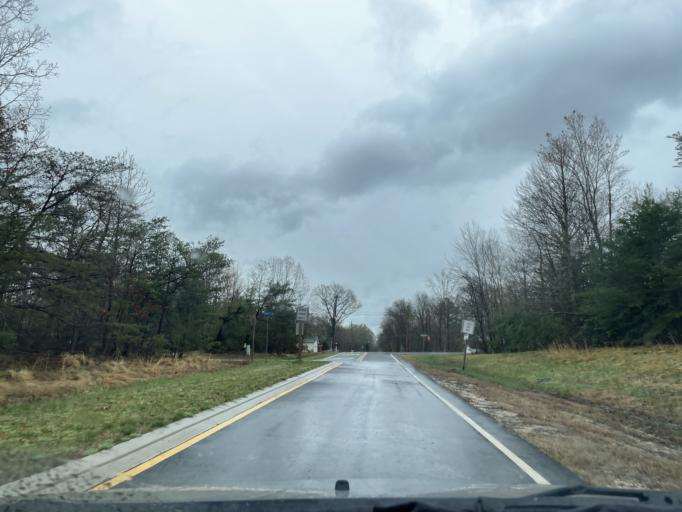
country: US
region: Maryland
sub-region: Saint Mary's County
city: California
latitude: 38.3068
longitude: -76.5163
